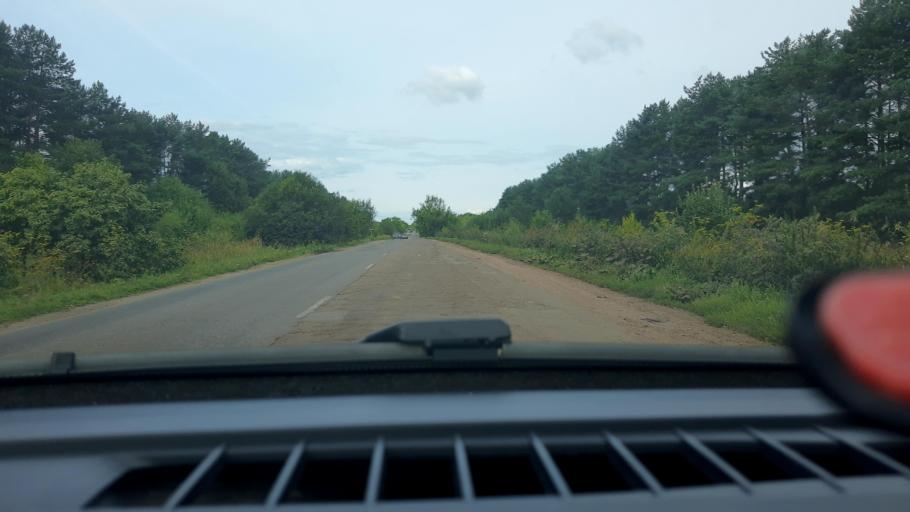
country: RU
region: Nizjnij Novgorod
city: Bogorodsk
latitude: 56.0660
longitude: 43.5948
